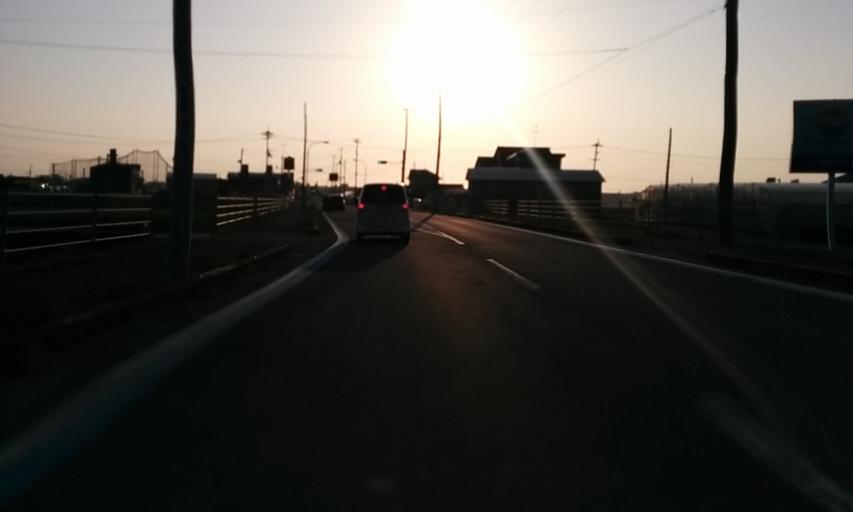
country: JP
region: Ehime
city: Masaki-cho
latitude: 33.7715
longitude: 132.7291
